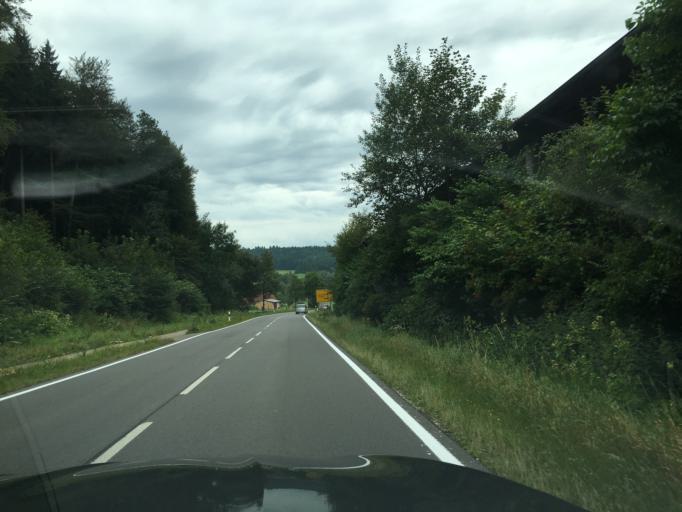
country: DE
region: Baden-Wuerttemberg
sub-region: Tuebingen Region
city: Rot
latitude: 47.8600
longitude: 9.1053
